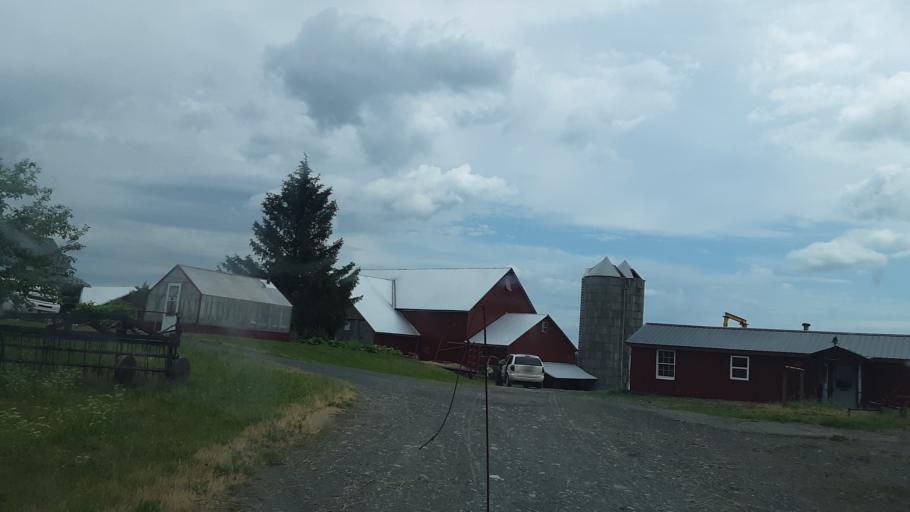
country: US
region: Maine
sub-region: Aroostook County
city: Fort Fairfield
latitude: 46.6961
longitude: -67.8471
